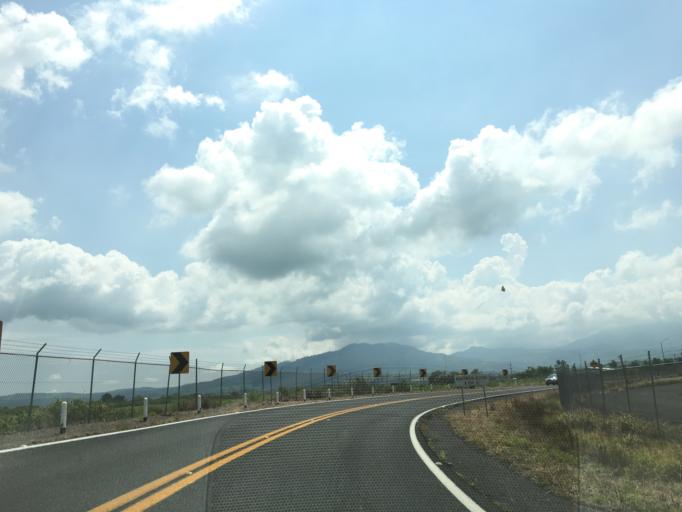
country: MX
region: Nayarit
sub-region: Tepic
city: La Corregidora
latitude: 21.4158
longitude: -104.8338
